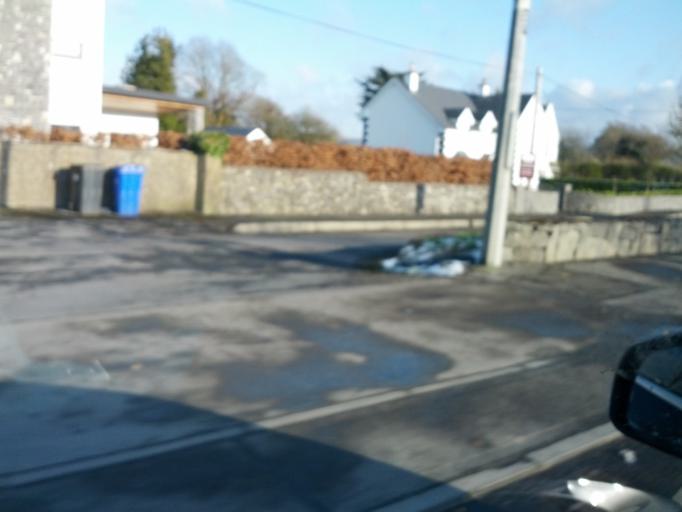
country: IE
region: Connaught
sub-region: County Galway
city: Gort
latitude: 53.1561
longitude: -8.8057
